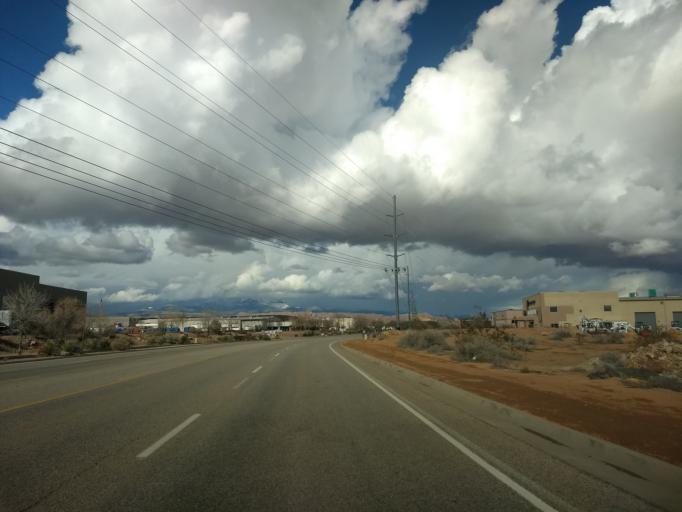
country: US
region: Utah
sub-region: Washington County
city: Saint George
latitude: 37.0333
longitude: -113.5615
